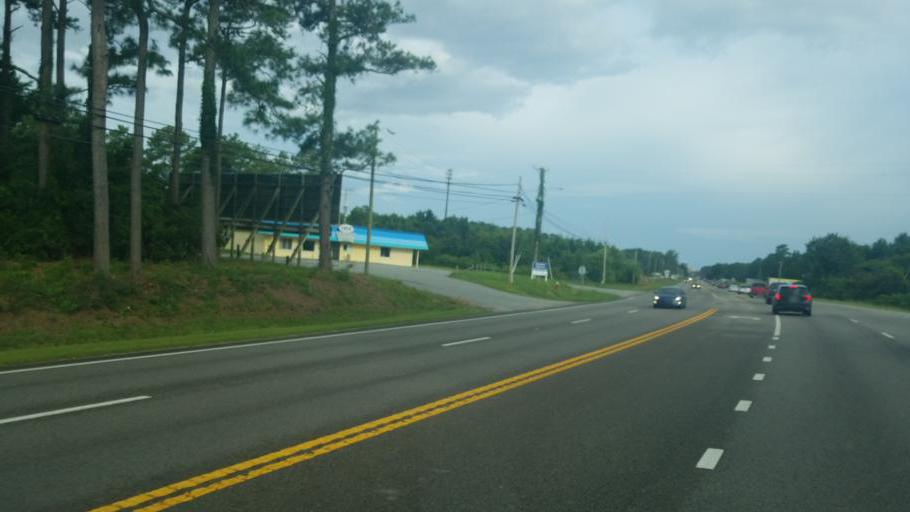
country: US
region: North Carolina
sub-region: Dare County
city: Southern Shores
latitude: 36.1018
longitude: -75.8143
